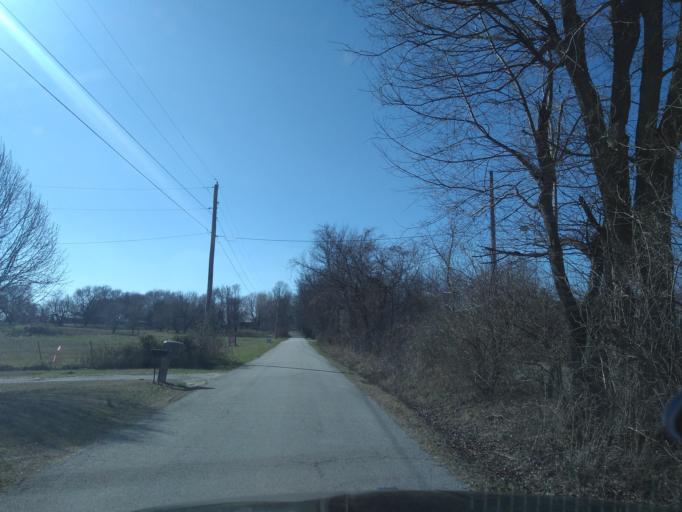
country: US
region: Arkansas
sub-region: Washington County
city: Farmington
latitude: 36.0678
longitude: -94.2460
